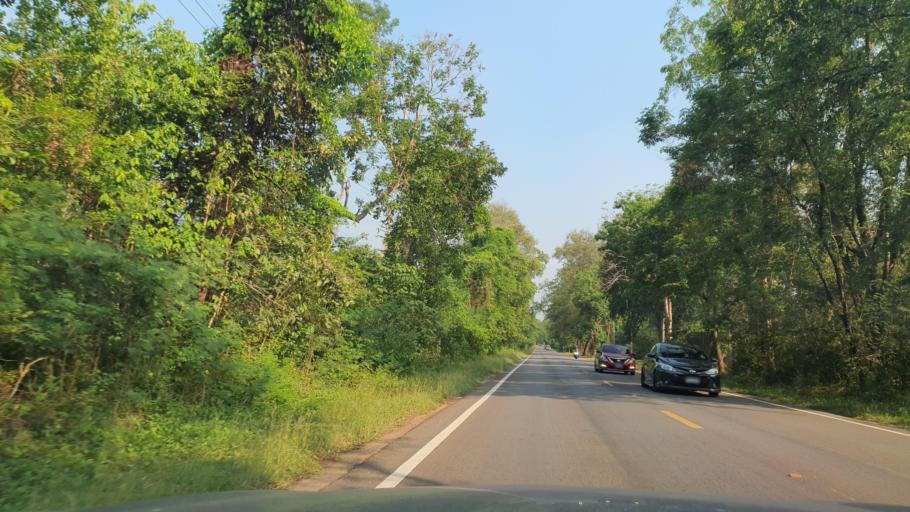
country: TH
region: Kanchanaburi
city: Sai Yok
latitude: 14.2698
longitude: 99.2349
